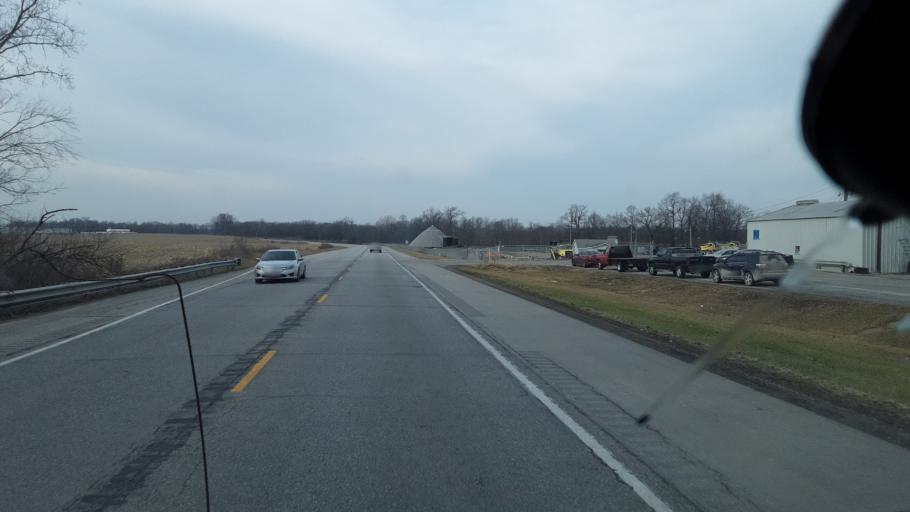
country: US
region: Indiana
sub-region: DeKalb County
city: Waterloo
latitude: 41.4366
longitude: -85.0341
